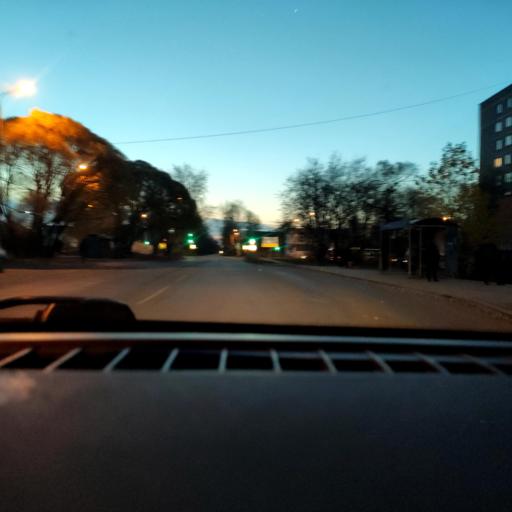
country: RU
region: Perm
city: Perm
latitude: 58.0623
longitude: 56.3601
